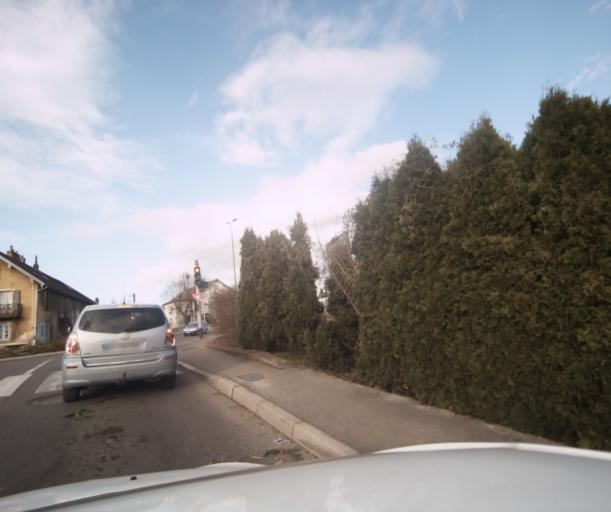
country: FR
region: Franche-Comte
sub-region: Departement du Doubs
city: Besancon
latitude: 47.2591
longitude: 6.0286
